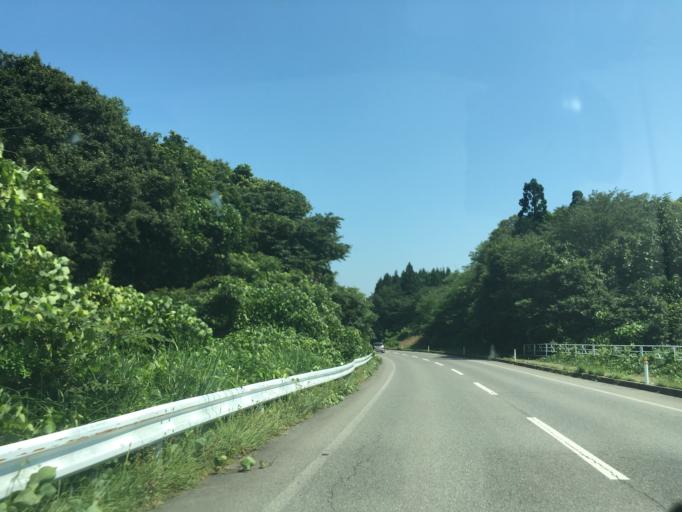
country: JP
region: Akita
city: Tenno
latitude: 39.9693
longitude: 139.7462
